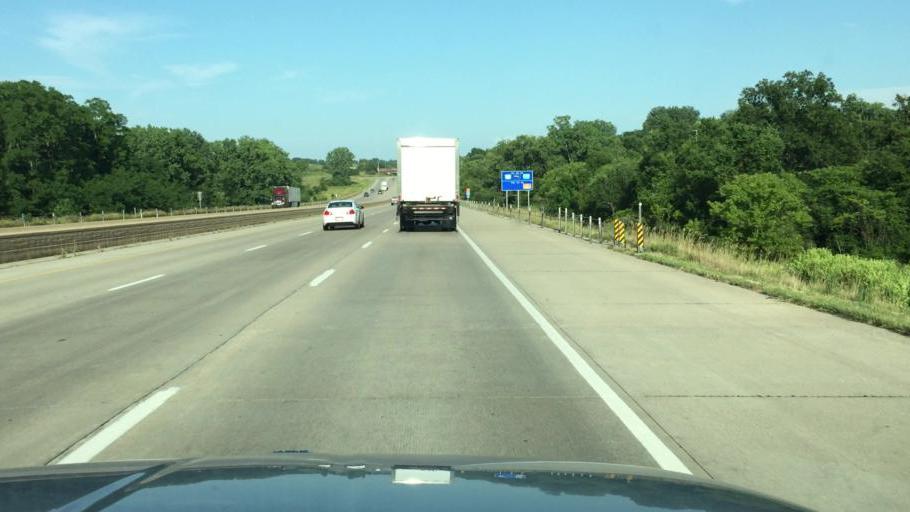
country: US
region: Iowa
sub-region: Johnson County
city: Iowa City
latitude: 41.6869
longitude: -91.5114
